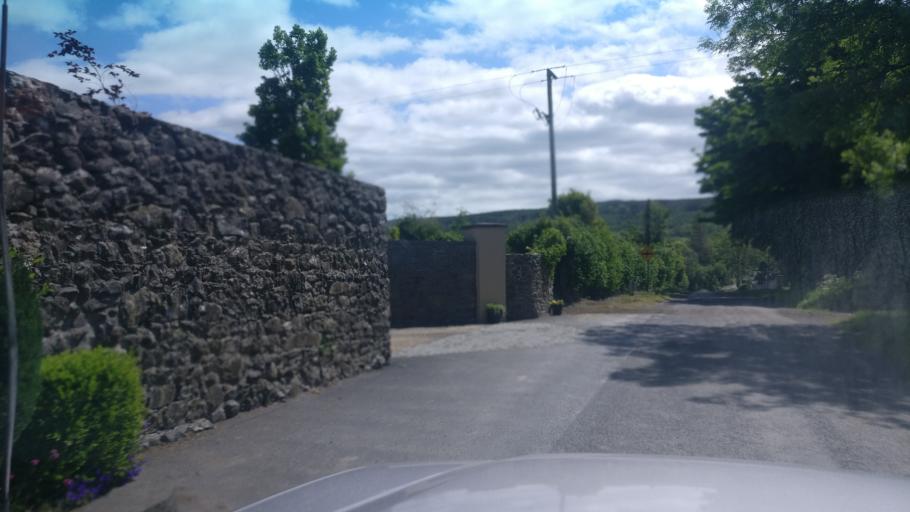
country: IE
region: Connaught
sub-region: County Galway
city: Gort
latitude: 53.1368
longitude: -8.7174
